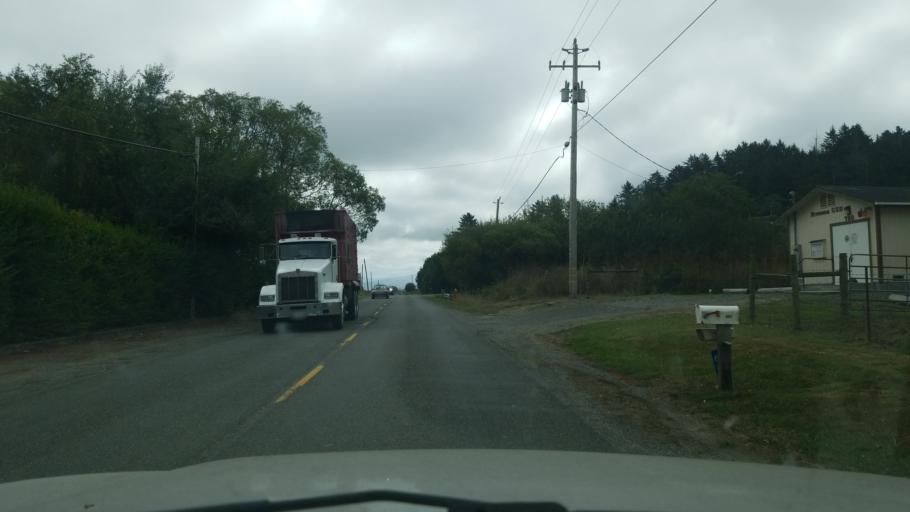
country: US
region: California
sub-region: Humboldt County
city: Ferndale
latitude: 40.5811
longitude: -124.2816
